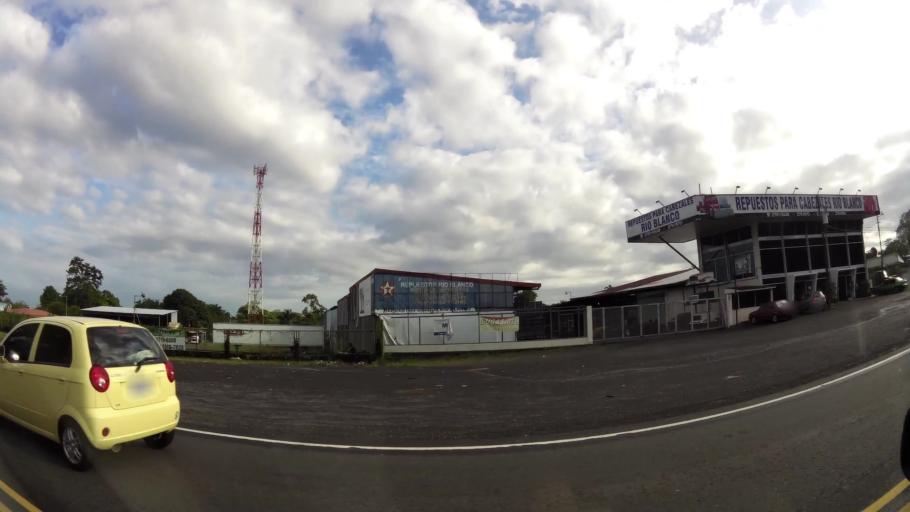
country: CR
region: Limon
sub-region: Canton de Pococi
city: Guapiles
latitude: 10.2114
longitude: -83.8365
